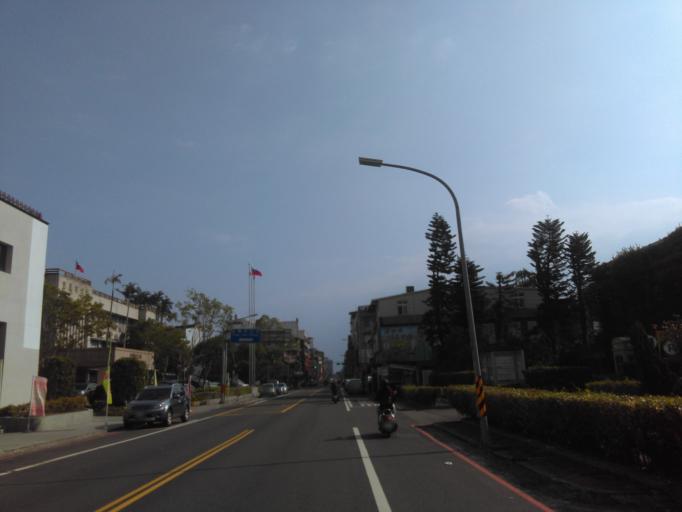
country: TW
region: Taiwan
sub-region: Yilan
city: Yilan
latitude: 24.7524
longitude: 121.7529
